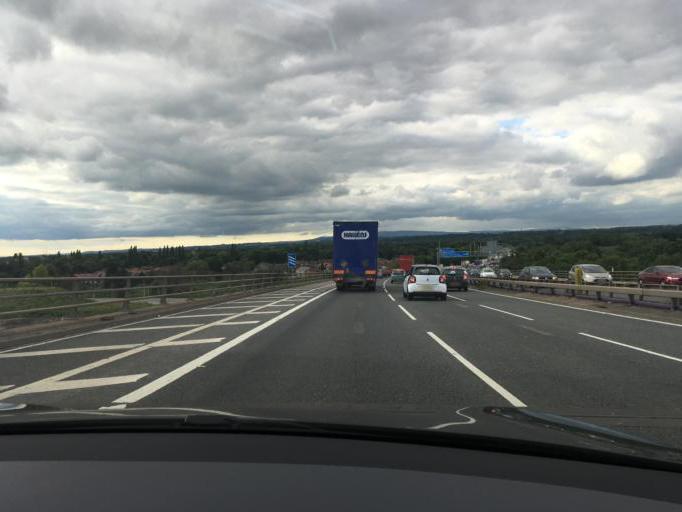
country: GB
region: England
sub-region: Trafford
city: Urmston
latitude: 53.4704
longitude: -2.3705
